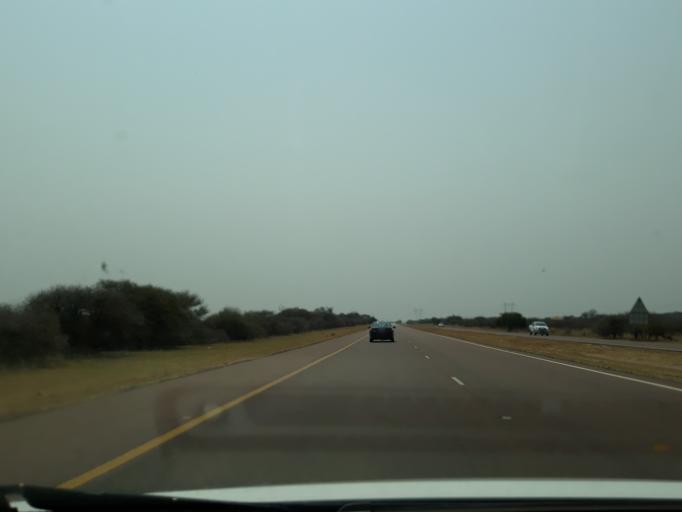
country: BW
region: Kgatleng
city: Mochudi
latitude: -24.3618
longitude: 26.0707
